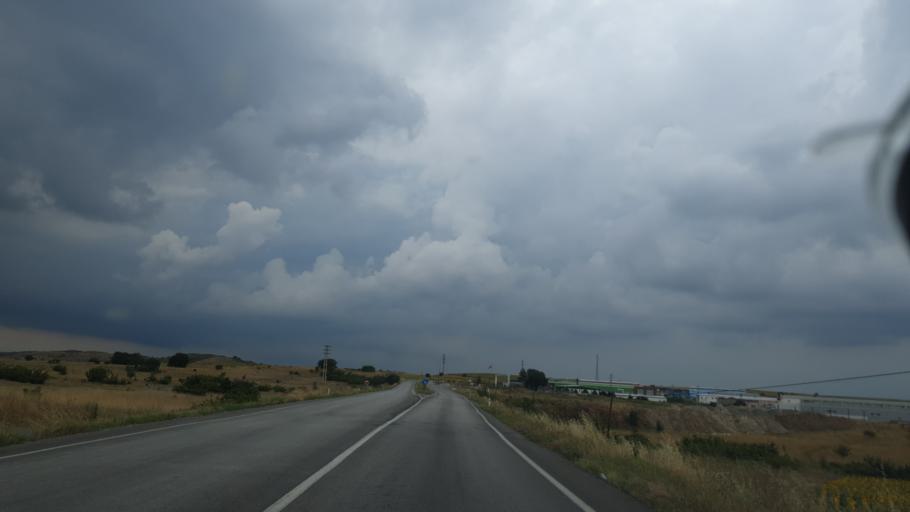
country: TR
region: Tekirdag
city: Hayrabolu
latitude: 41.2205
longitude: 27.0503
